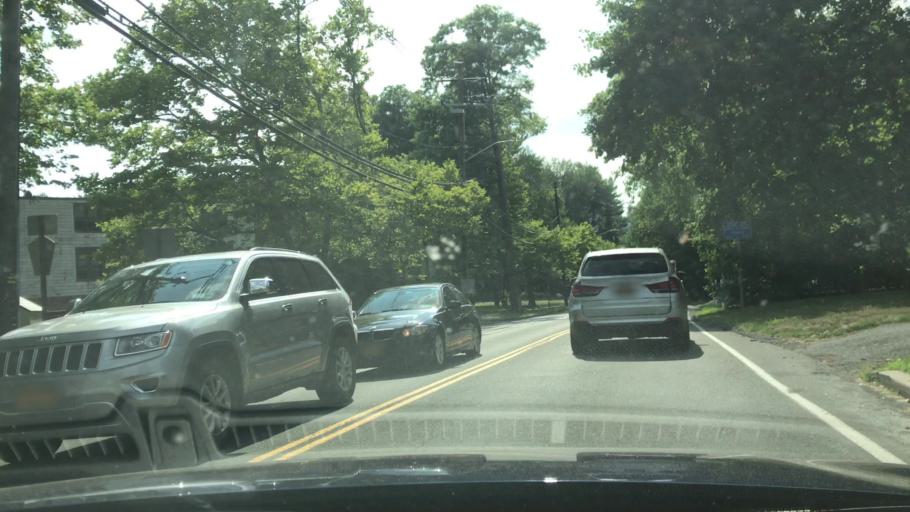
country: US
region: New York
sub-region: Rockland County
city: Bardonia
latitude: 41.1123
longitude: -74.0110
